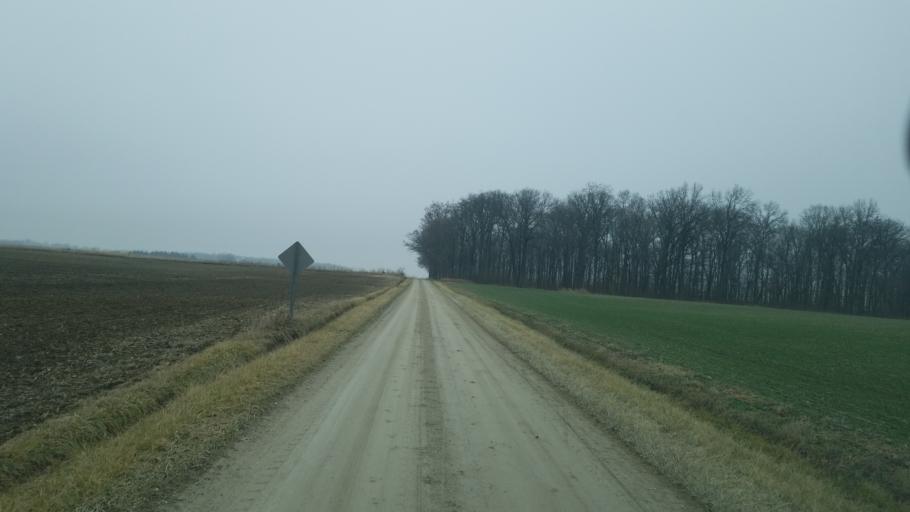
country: US
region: Indiana
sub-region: Adams County
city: Geneva
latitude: 40.5770
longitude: -84.8587
